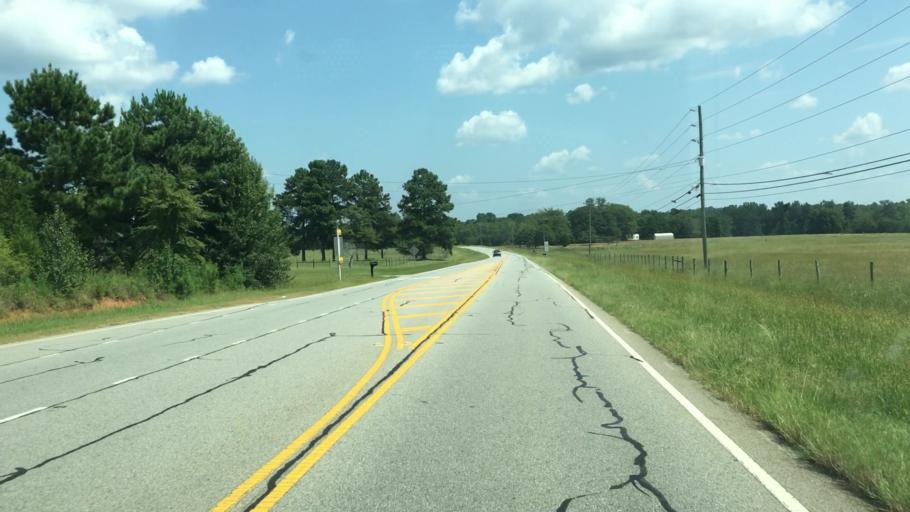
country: US
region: Georgia
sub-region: Oconee County
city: Bogart
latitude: 33.8744
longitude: -83.5246
